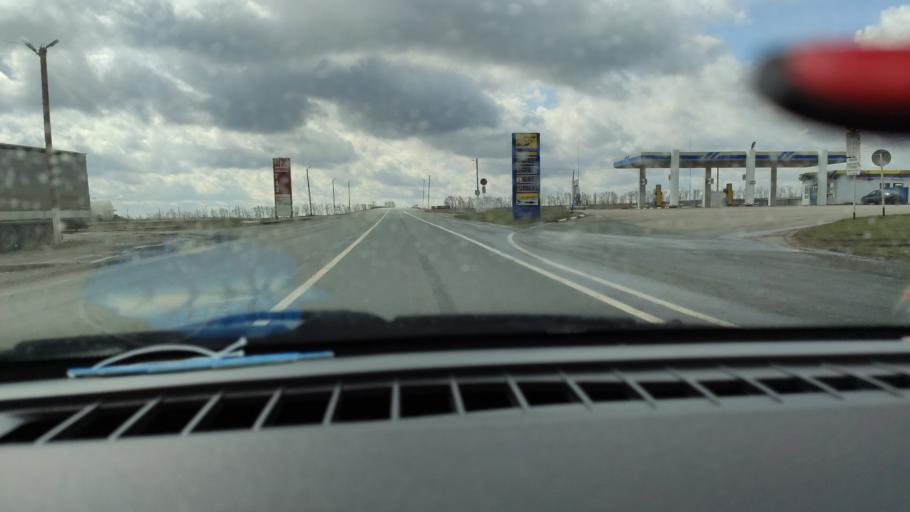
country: RU
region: Samara
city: Yelkhovka
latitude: 53.8685
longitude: 50.2583
